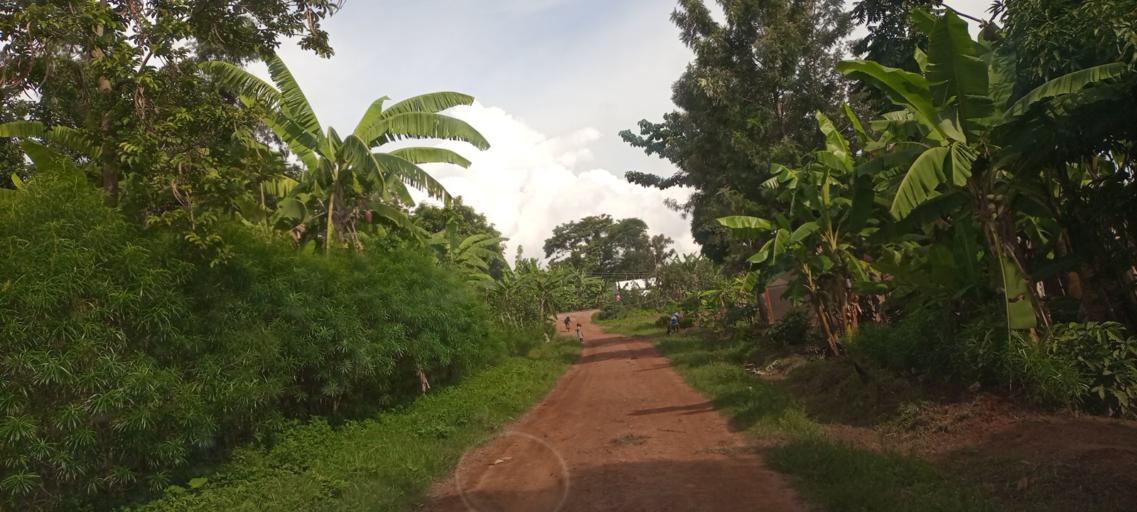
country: UG
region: Eastern Region
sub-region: Mbale District
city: Mbale
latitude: 1.1352
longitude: 34.1760
